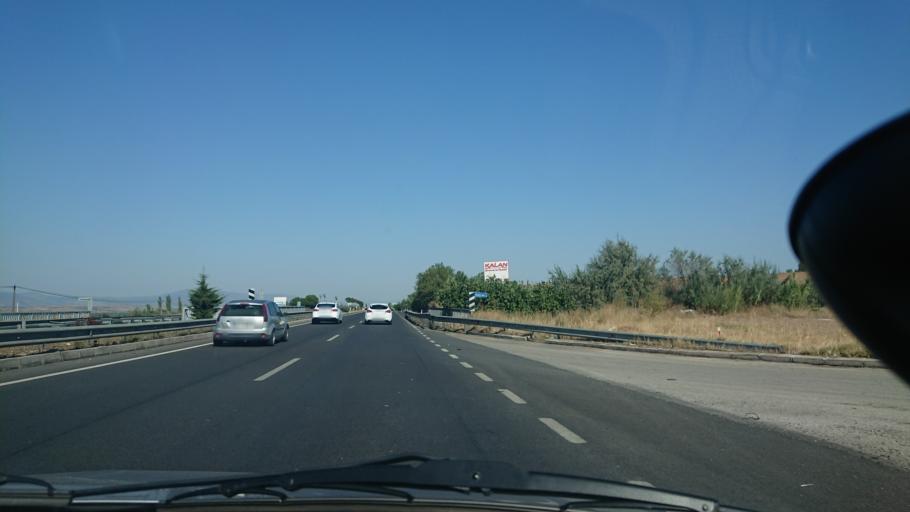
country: TR
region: Manisa
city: Ahmetli
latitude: 38.5096
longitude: 27.9045
